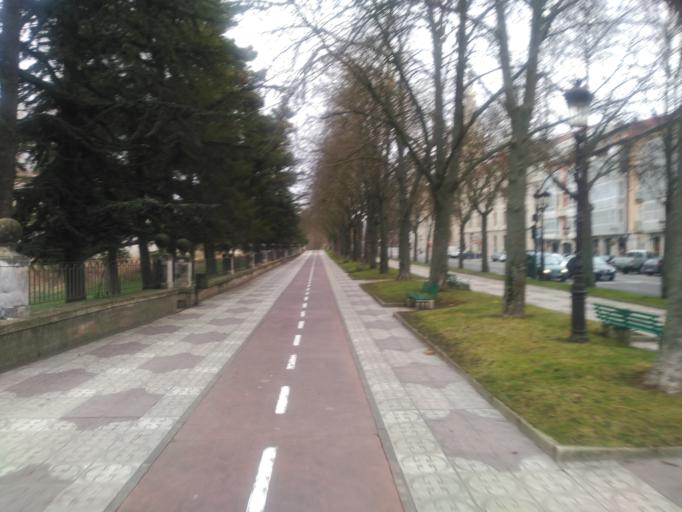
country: ES
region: Castille and Leon
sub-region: Provincia de Burgos
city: Burgos
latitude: 42.3378
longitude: -3.7053
